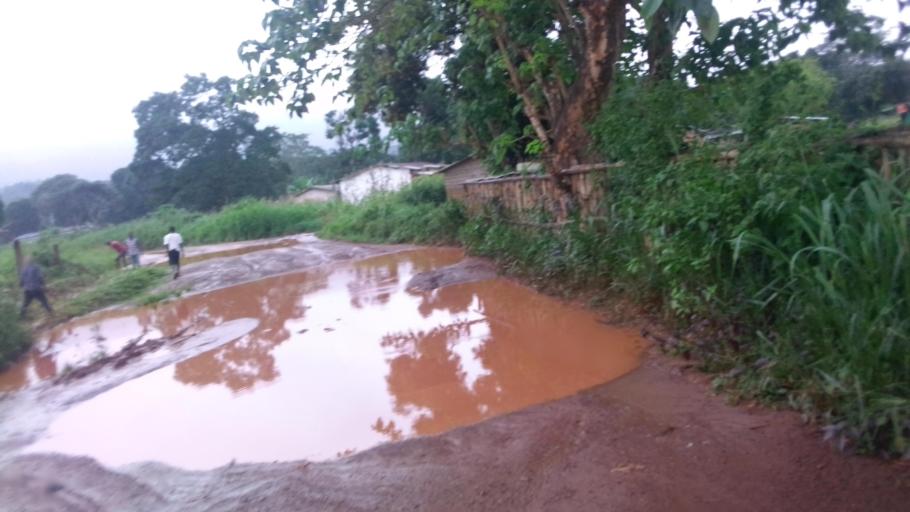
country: SL
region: Eastern Province
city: Hangha
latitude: 7.9135
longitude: -11.1687
